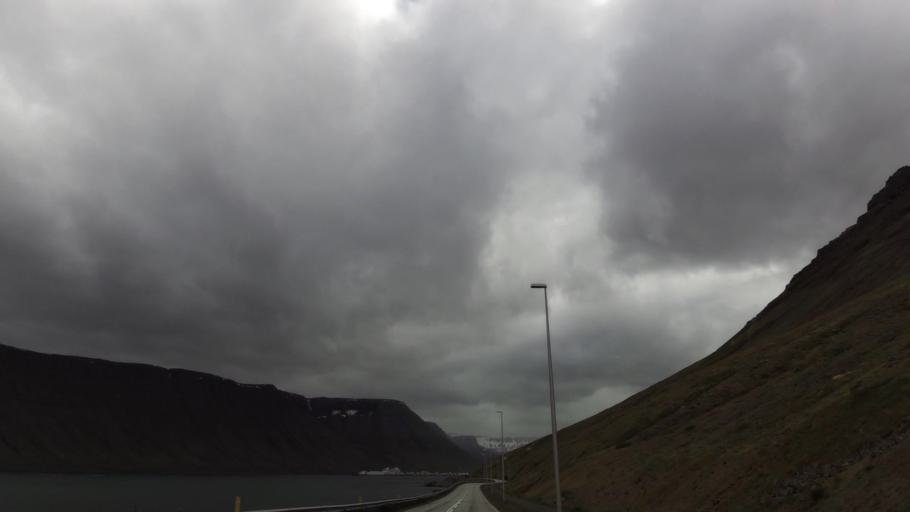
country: IS
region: Westfjords
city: Isafjoerdur
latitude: 66.0978
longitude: -23.1107
